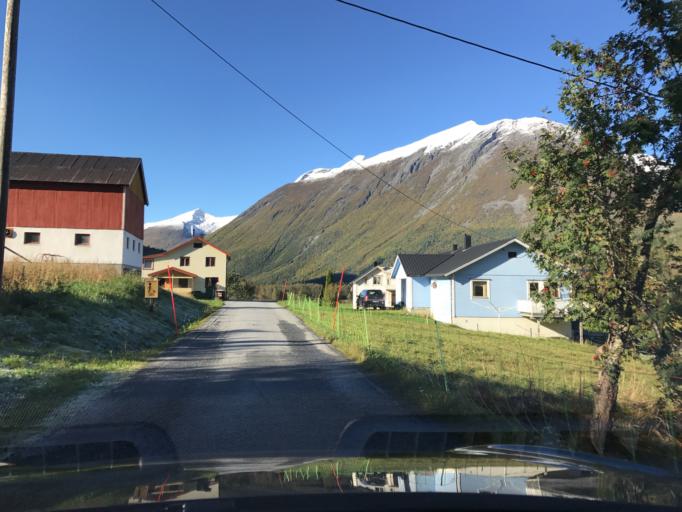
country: NO
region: More og Romsdal
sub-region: Norddal
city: Valldal
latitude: 62.3304
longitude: 7.3801
